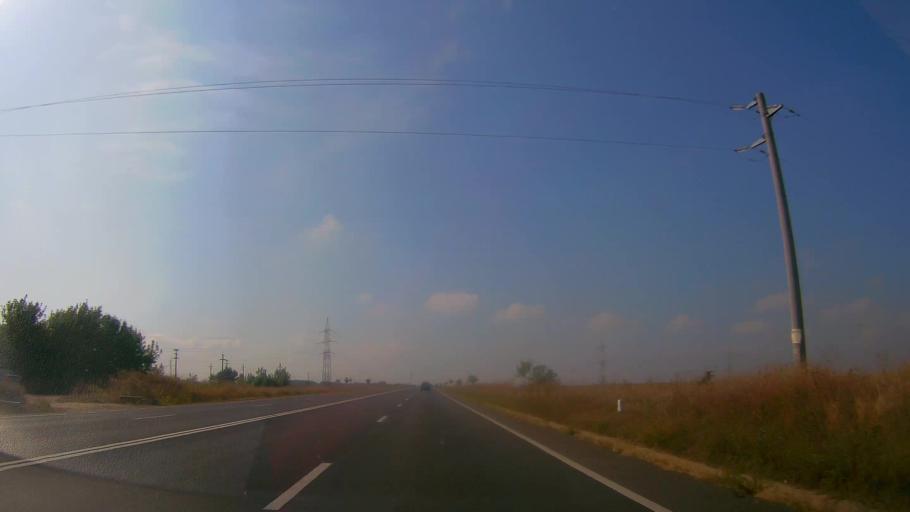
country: RO
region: Giurgiu
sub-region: Comuna Calugareni
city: Uzunu
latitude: 44.1361
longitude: 25.9940
